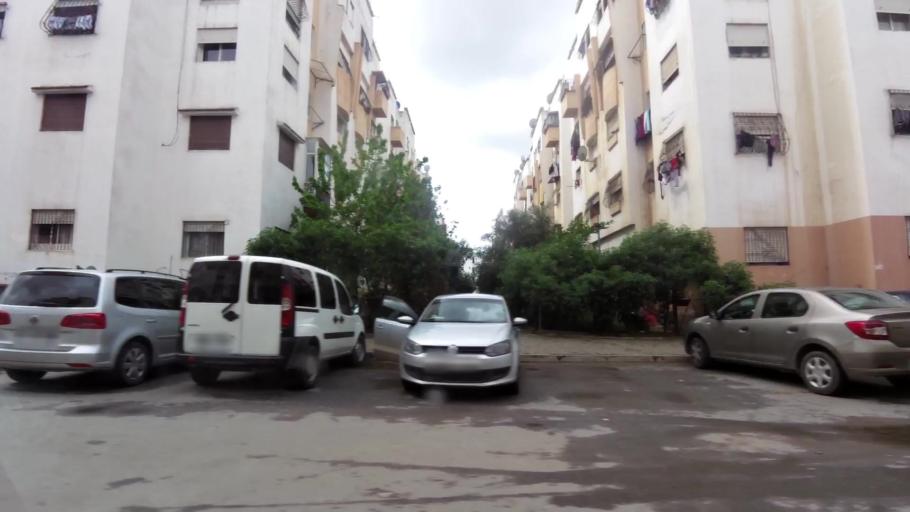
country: MA
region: Grand Casablanca
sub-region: Nouaceur
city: Bouskoura
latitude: 33.5215
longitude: -7.6454
